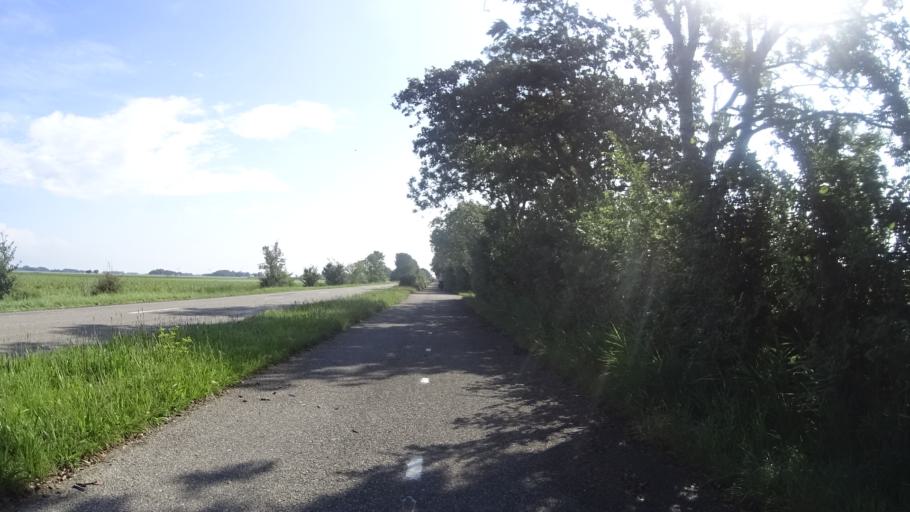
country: NL
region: Friesland
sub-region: Gemeente Franekeradeel
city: Tzum
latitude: 53.1927
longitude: 5.5941
